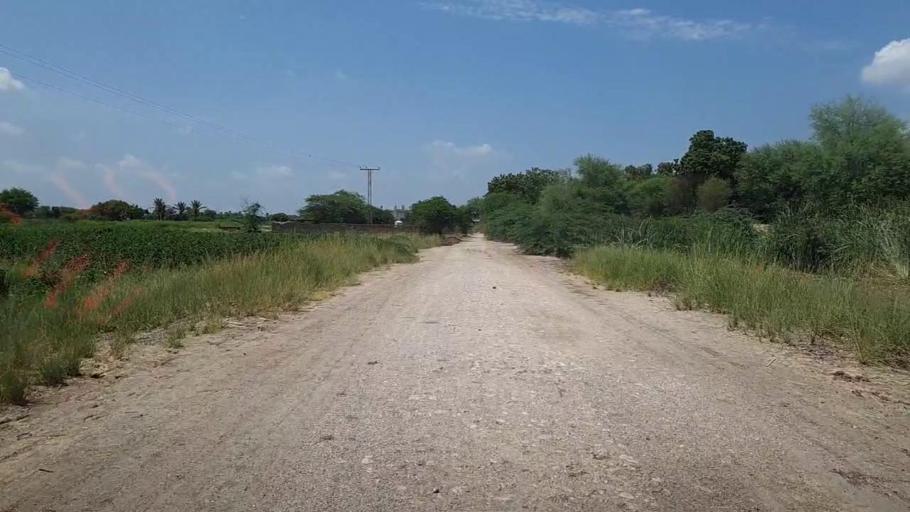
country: PK
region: Sindh
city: Kandiaro
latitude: 26.9821
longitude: 68.2436
